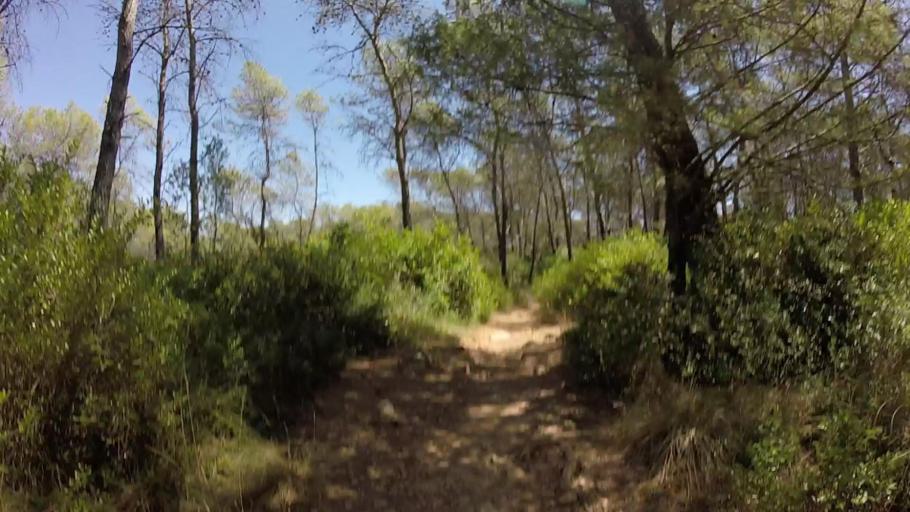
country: FR
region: Provence-Alpes-Cote d'Azur
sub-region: Departement des Alpes-Maritimes
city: Vallauris
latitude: 43.6086
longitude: 7.0513
